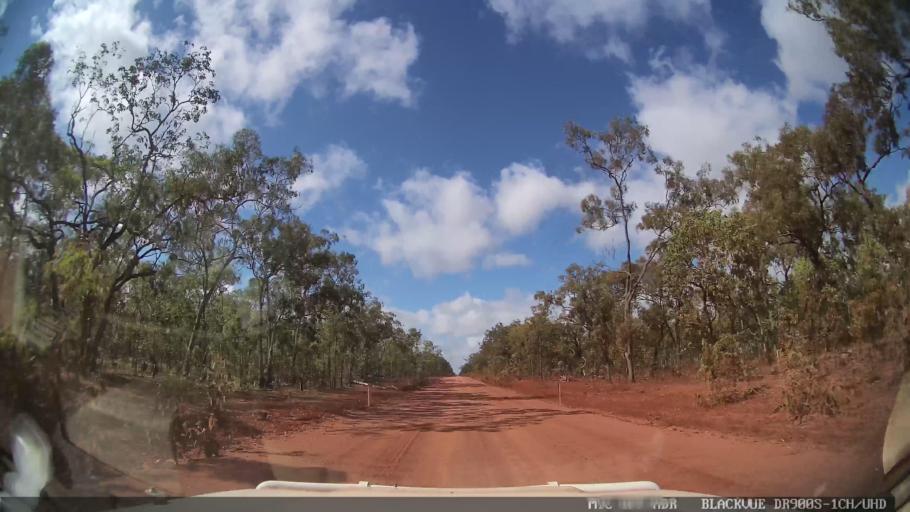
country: AU
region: Queensland
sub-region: Cook
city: Weipa
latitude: -12.2072
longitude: 142.5821
